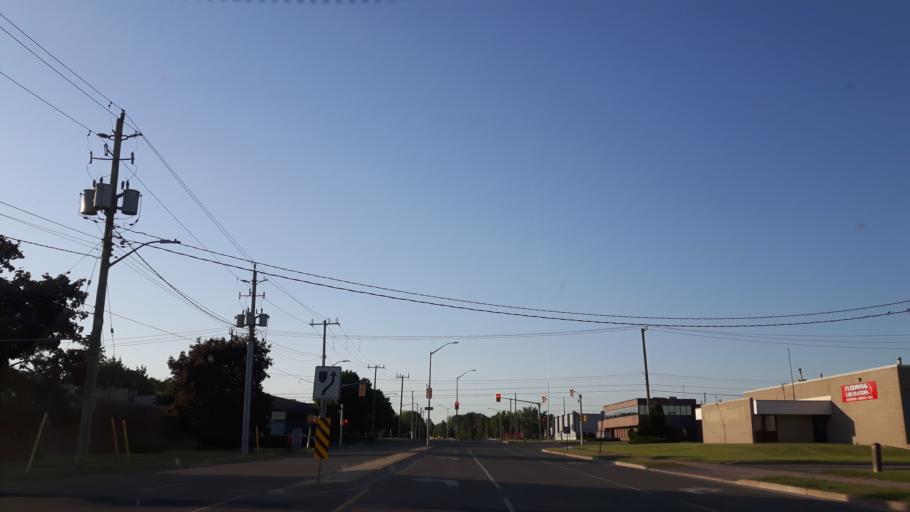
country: CA
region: Ontario
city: London
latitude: 42.9336
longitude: -81.2080
